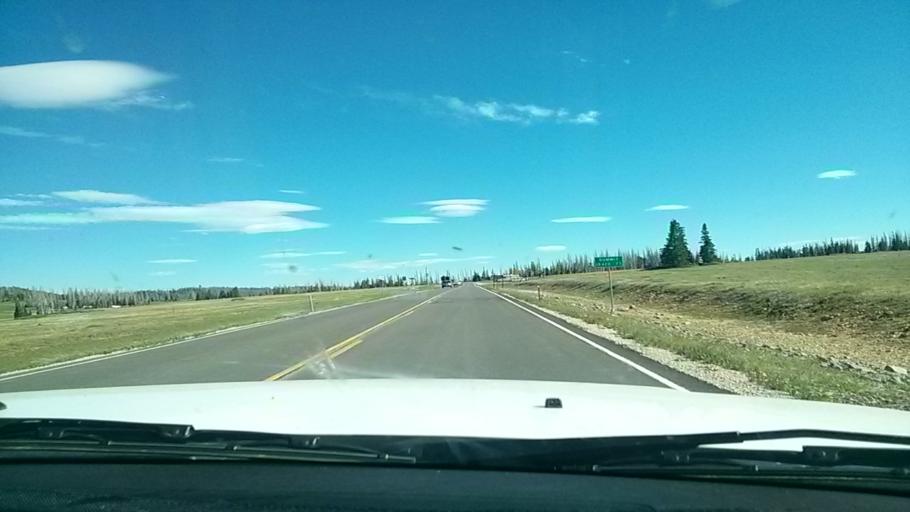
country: US
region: Utah
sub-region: Iron County
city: Parowan
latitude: 37.6656
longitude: -112.8382
